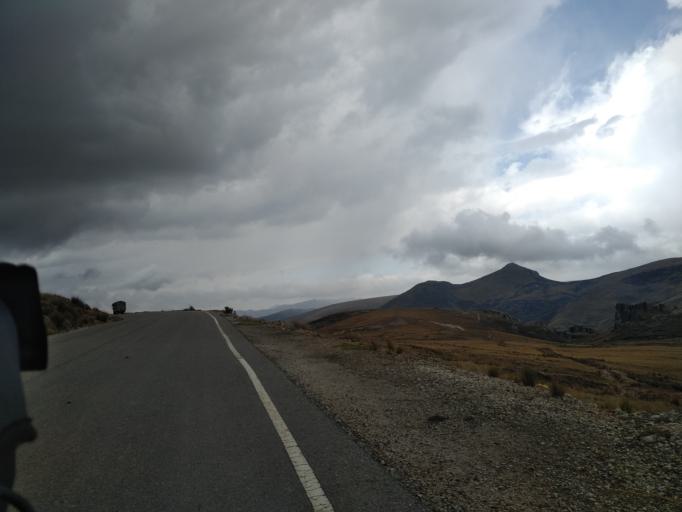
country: PE
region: La Libertad
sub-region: Provincia de Santiago de Chuco
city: Quiruvilca
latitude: -7.9931
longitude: -78.2989
